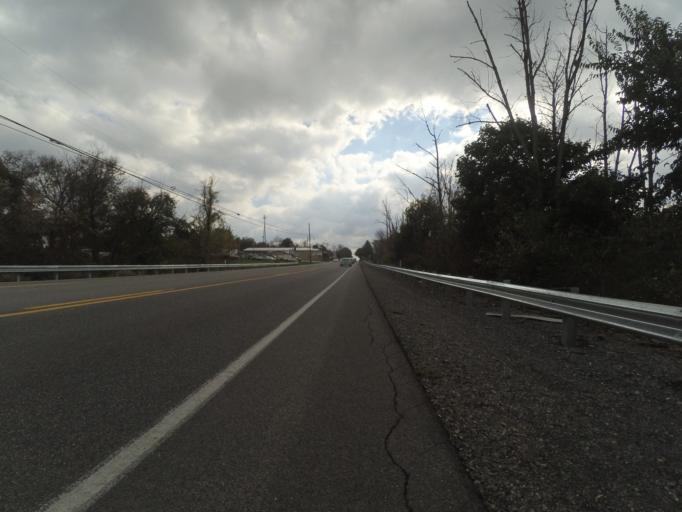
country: US
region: Pennsylvania
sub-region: Centre County
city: Bellefonte
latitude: 40.8949
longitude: -77.7867
